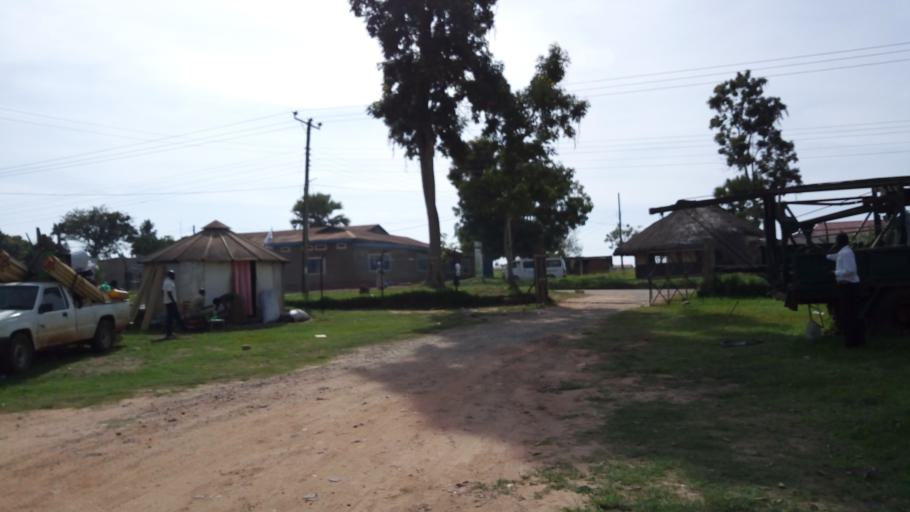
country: UG
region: Northern Region
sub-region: Arua District
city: Arua
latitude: 3.0180
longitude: 30.9097
